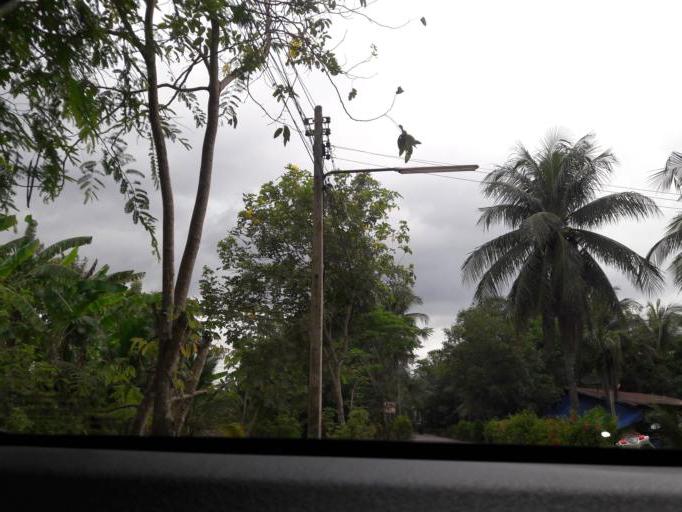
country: TH
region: Ratchaburi
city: Damnoen Saduak
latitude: 13.5732
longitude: 99.9944
